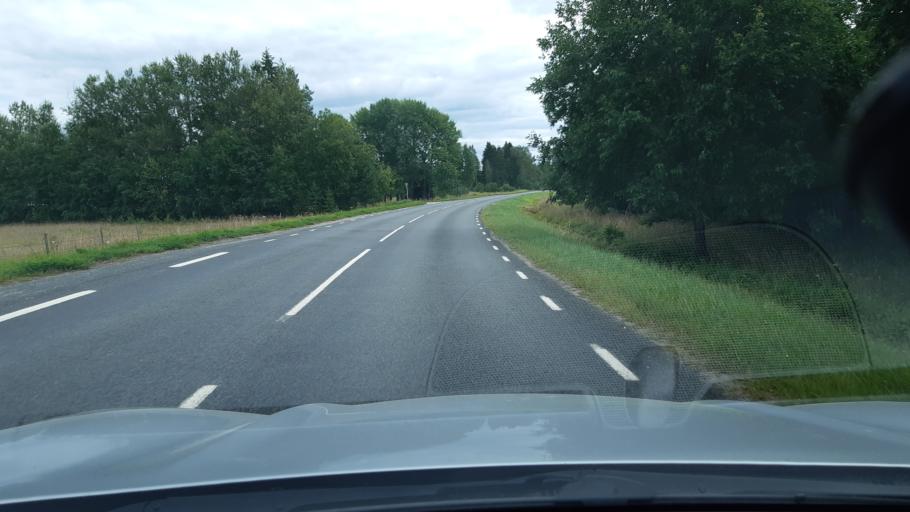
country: EE
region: Raplamaa
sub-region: Maerjamaa vald
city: Marjamaa
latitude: 59.0453
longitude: 24.4795
